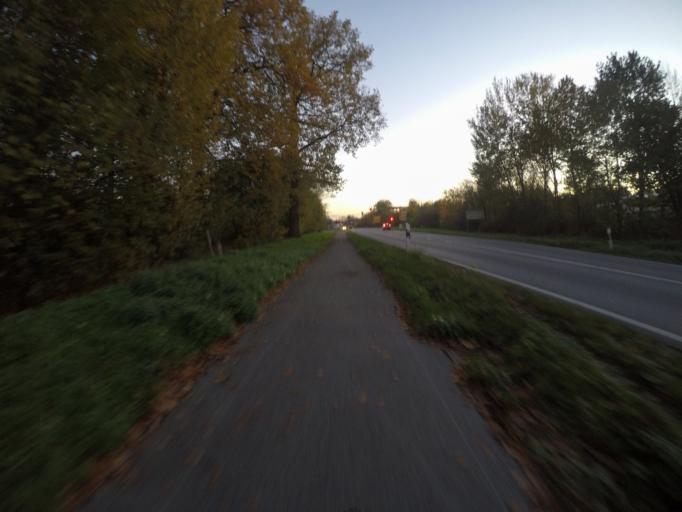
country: DE
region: North Rhine-Westphalia
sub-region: Regierungsbezirk Dusseldorf
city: Bocholt
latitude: 51.8128
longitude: 6.5696
